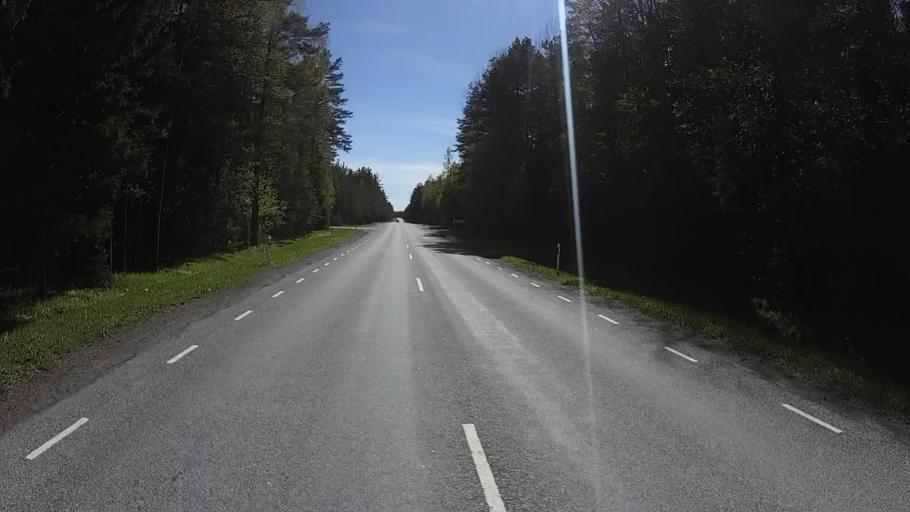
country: EE
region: Harju
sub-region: Loksa linn
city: Loksa
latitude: 59.5181
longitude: 25.6868
